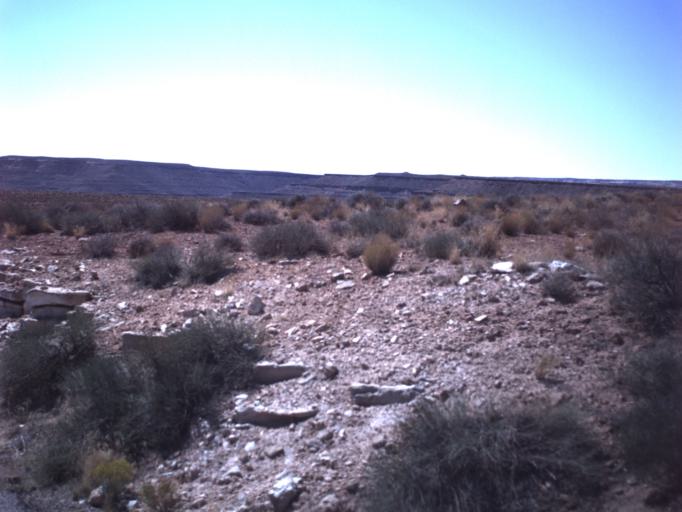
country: US
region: Arizona
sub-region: Navajo County
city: Kayenta
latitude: 37.1782
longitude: -109.9245
